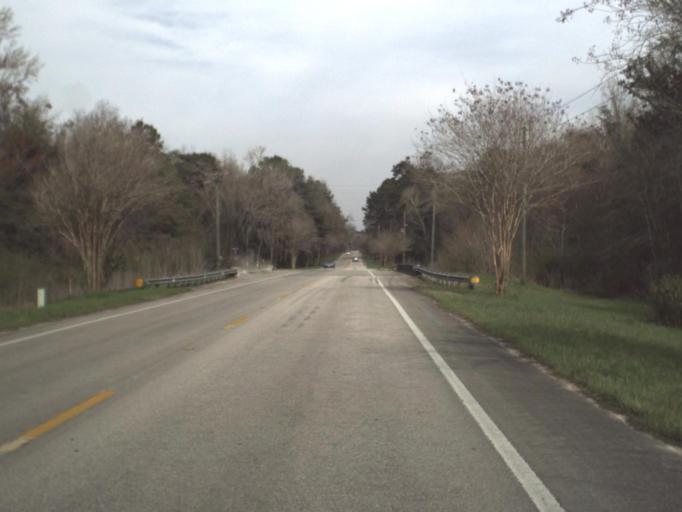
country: US
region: Florida
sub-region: Jefferson County
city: Monticello
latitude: 30.5423
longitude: -83.9053
